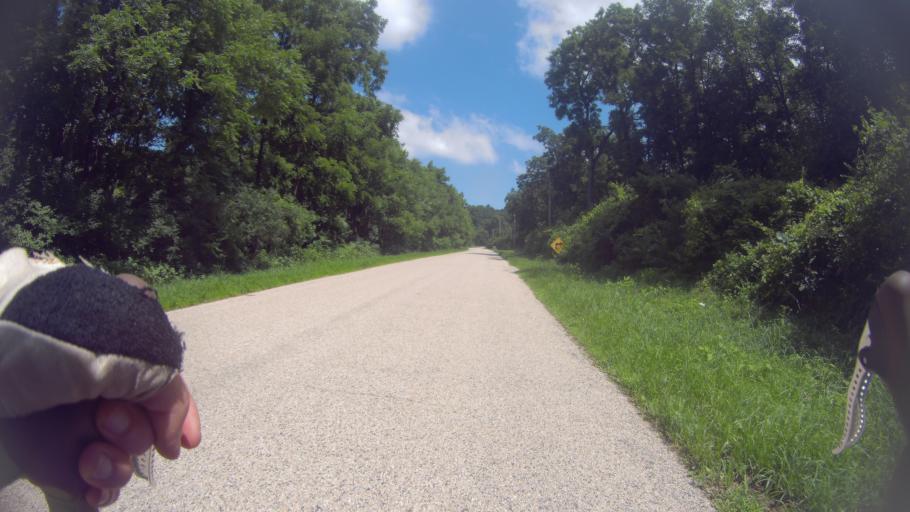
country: US
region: Wisconsin
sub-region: Sauk County
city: Sauk City
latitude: 43.2250
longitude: -89.6205
